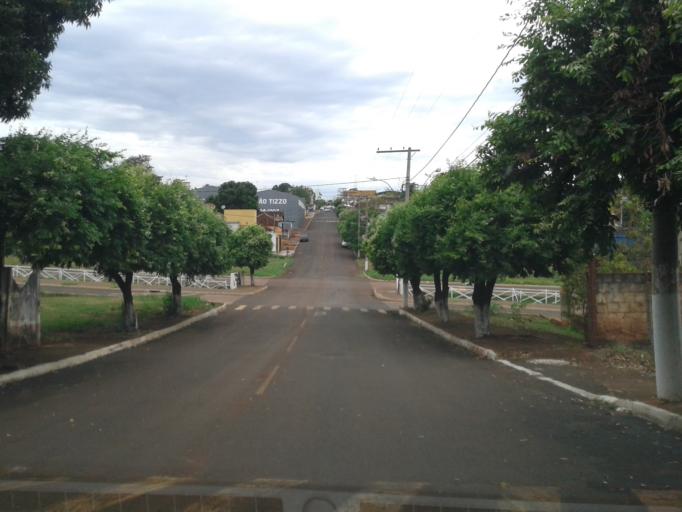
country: BR
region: Goias
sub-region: Itumbiara
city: Itumbiara
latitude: -18.4363
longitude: -49.1880
